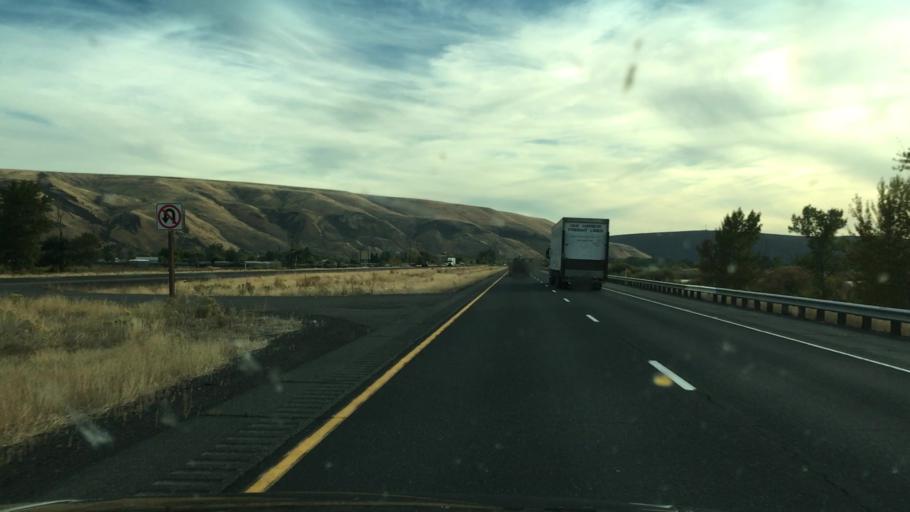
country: US
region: Washington
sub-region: Yakima County
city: Selah
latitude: 46.6655
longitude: -120.4918
